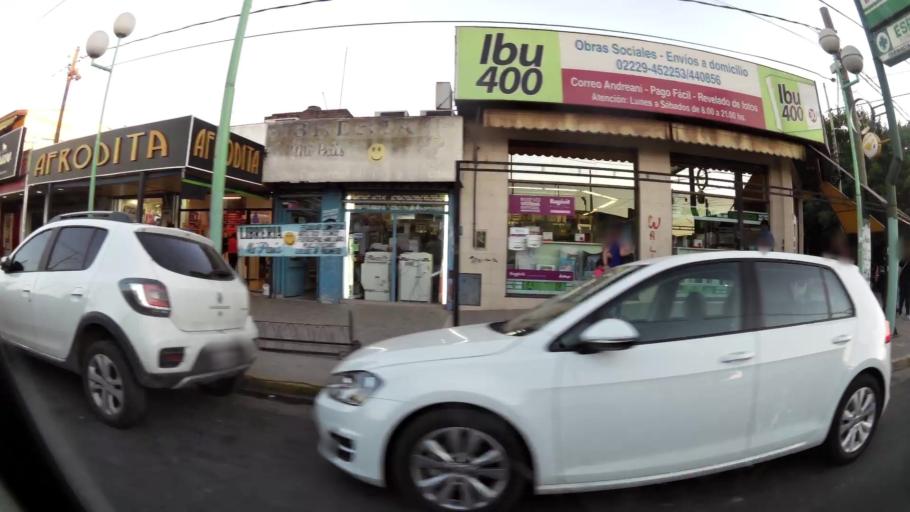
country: AR
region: Buenos Aires
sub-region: Partido de Quilmes
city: Quilmes
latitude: -34.8084
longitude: -58.1864
